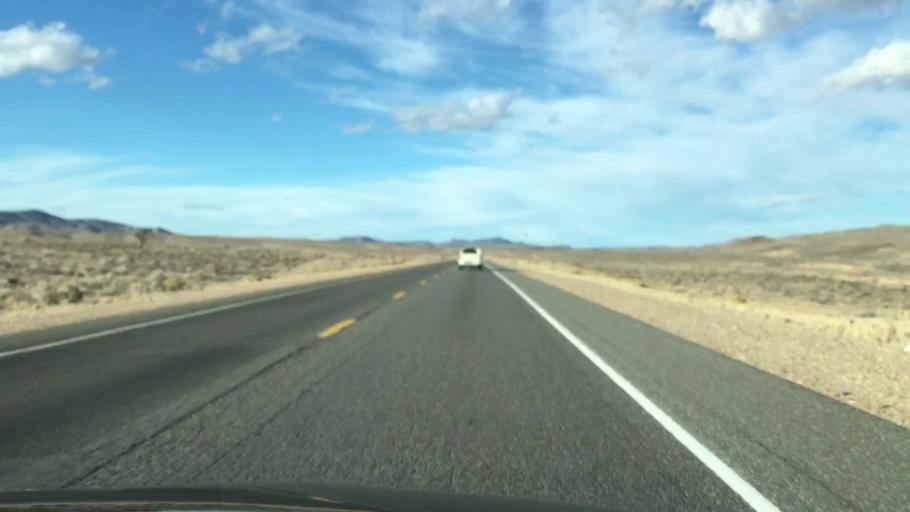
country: US
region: Nevada
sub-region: Esmeralda County
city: Goldfield
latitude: 37.5473
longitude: -117.1964
